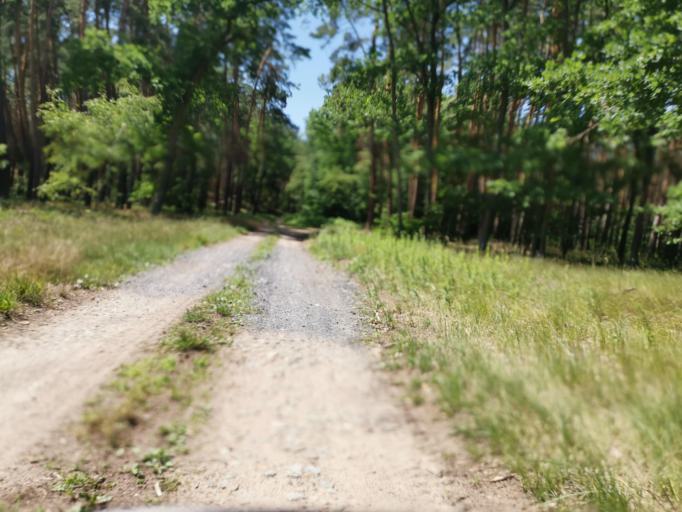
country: CZ
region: South Moravian
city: Bzenec
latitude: 48.9641
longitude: 17.2616
